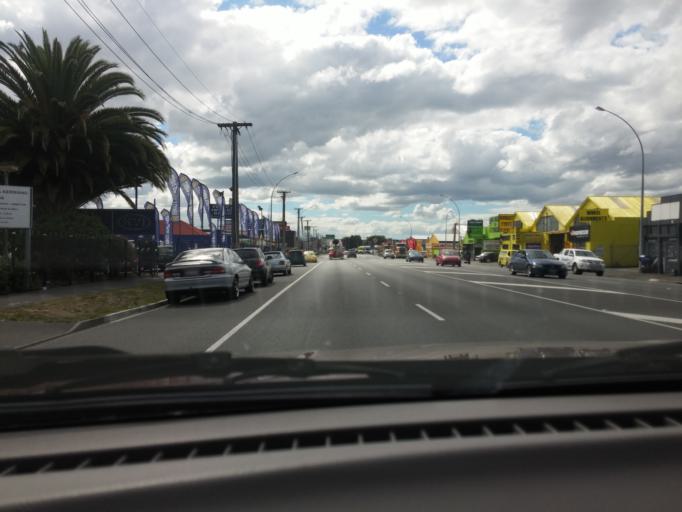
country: NZ
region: Waikato
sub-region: Hamilton City
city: Hamilton
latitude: -37.7930
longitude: 175.2602
